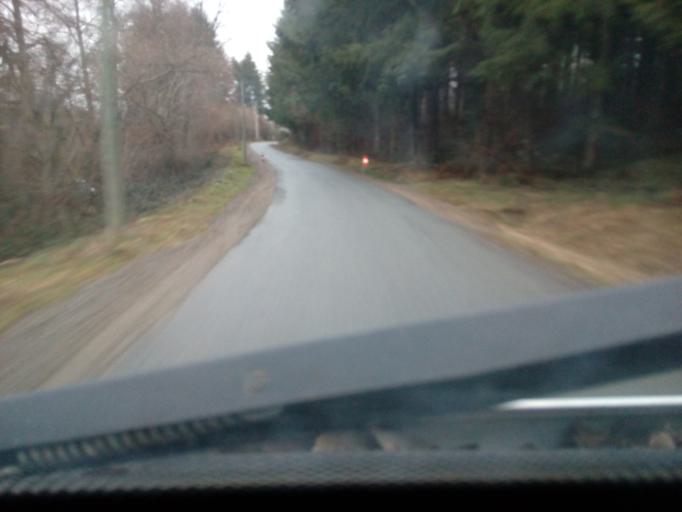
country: FR
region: Limousin
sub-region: Departement de la Creuse
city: Felletin
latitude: 45.8357
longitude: 2.2419
